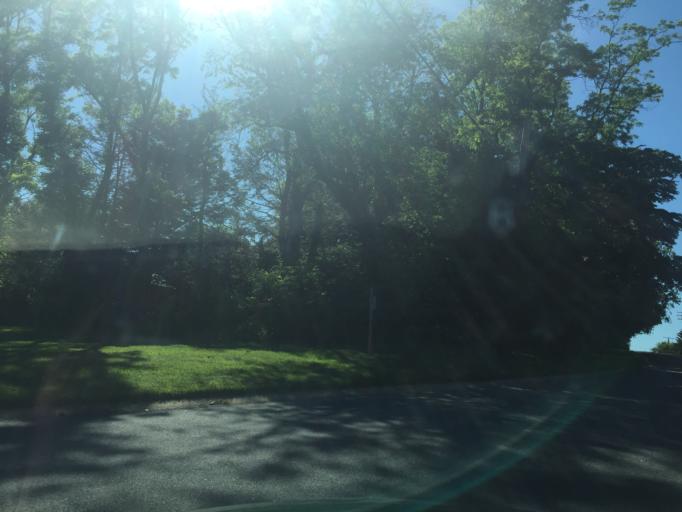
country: US
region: Maryland
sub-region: Baltimore County
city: Reisterstown
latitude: 39.5163
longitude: -76.9124
